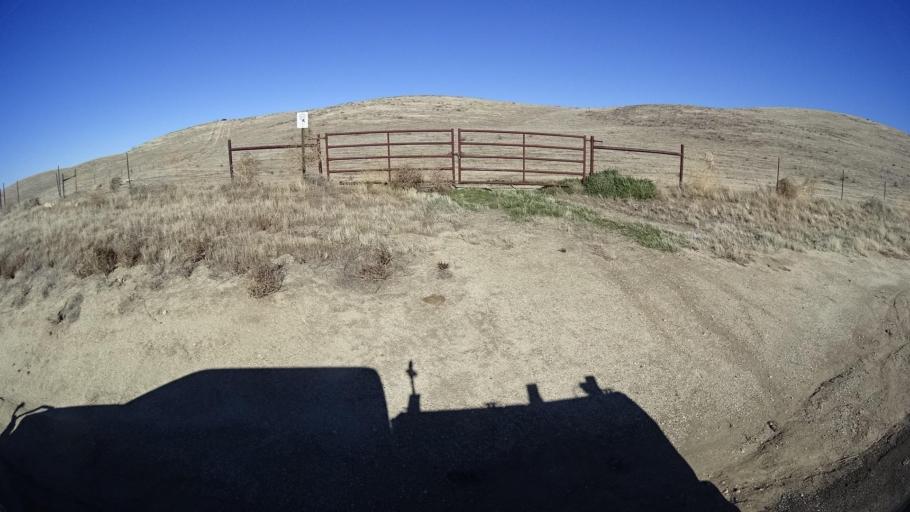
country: US
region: California
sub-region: Kern County
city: Maricopa
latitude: 34.9489
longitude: -119.4202
